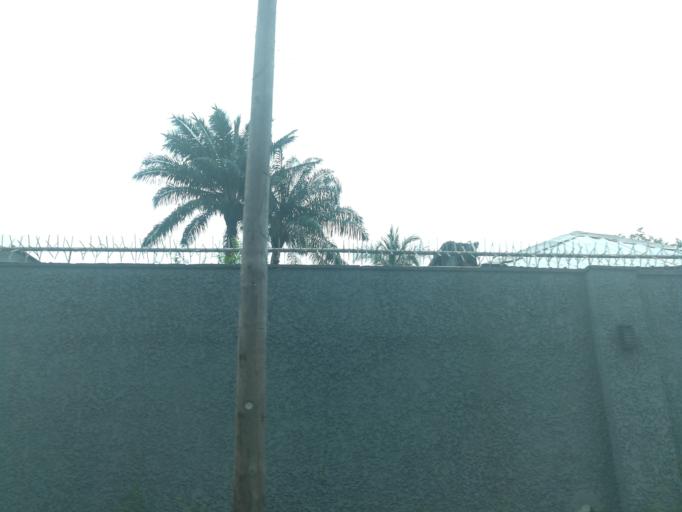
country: NG
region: Lagos
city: Ikoyi
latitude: 6.4318
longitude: 3.4147
